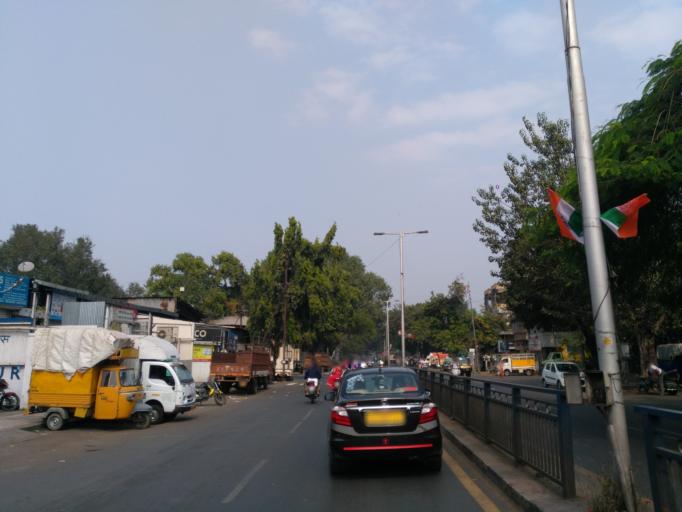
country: IN
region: Maharashtra
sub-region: Pune Division
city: Pune
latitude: 18.5079
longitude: 73.8683
